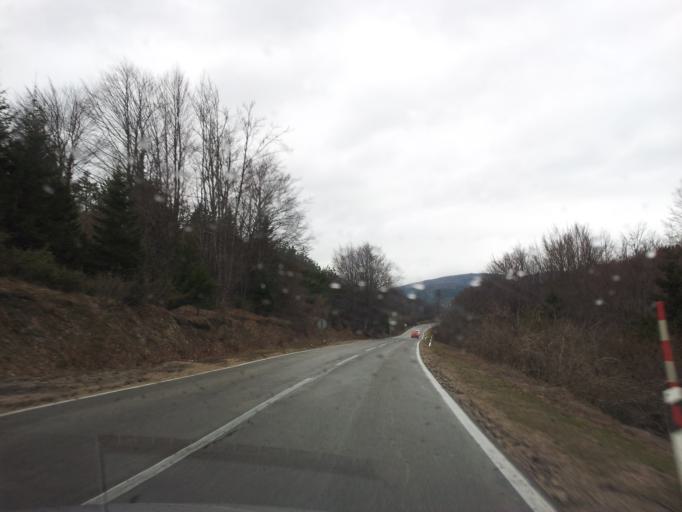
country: HR
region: Licko-Senjska
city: Jezerce
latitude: 44.7986
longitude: 15.6832
